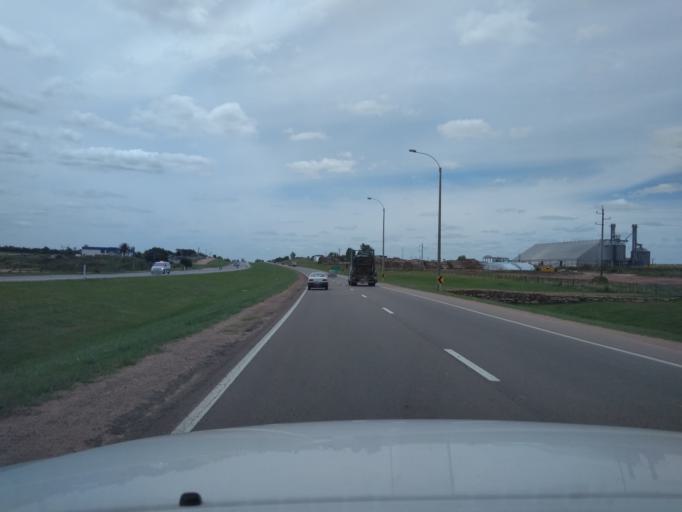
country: UY
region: Canelones
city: La Paz
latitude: -34.7475
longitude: -56.2535
